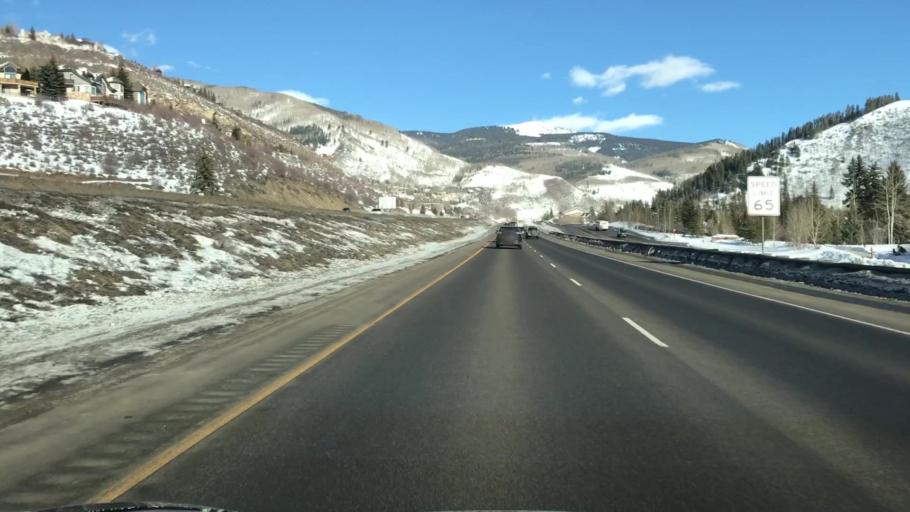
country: US
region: Colorado
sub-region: Eagle County
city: Vail
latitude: 39.6341
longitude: -106.4114
